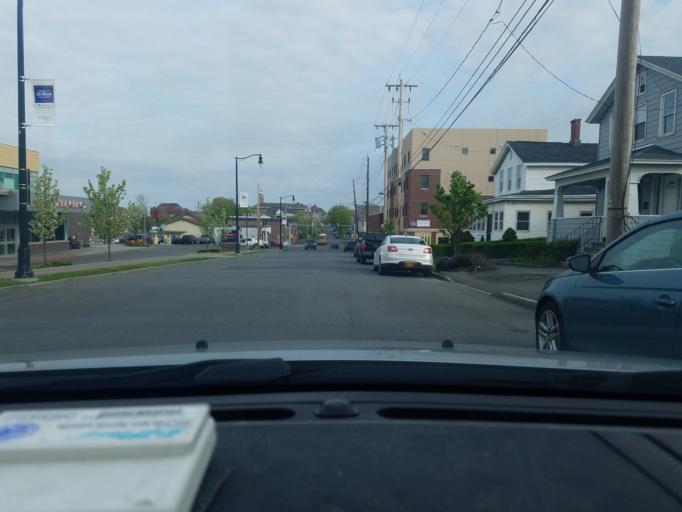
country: US
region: New York
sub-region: Onondaga County
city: Syracuse
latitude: 43.0584
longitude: -76.1497
